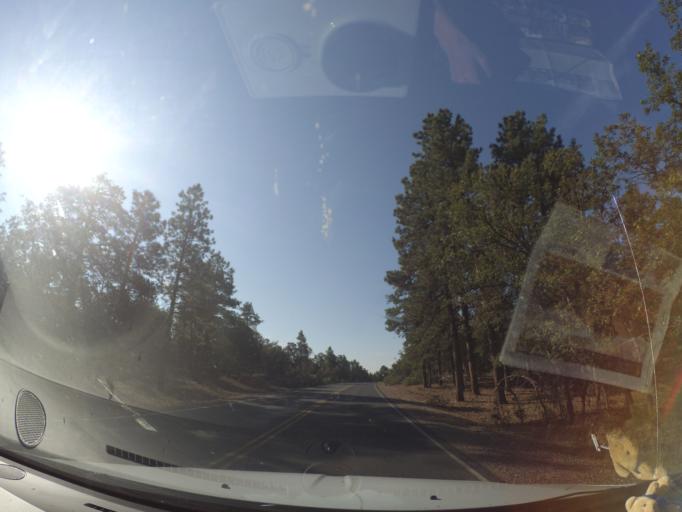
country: US
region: Arizona
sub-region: Coconino County
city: Grand Canyon
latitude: 36.0261
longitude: -112.0655
